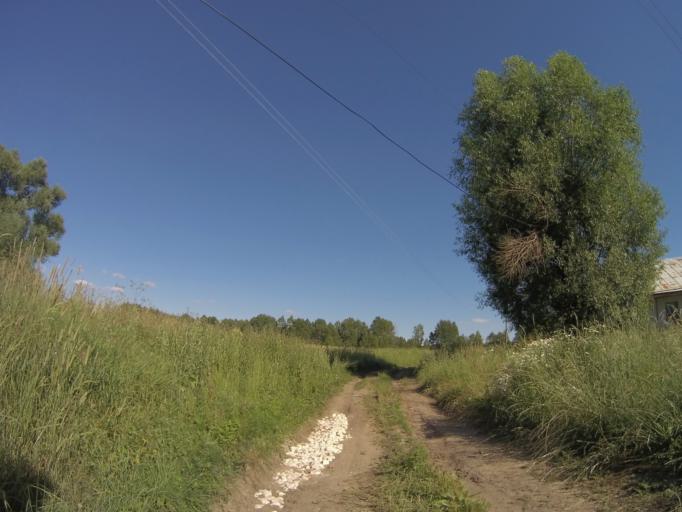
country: RU
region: Vladimir
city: Golovino
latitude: 56.0023
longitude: 40.3971
